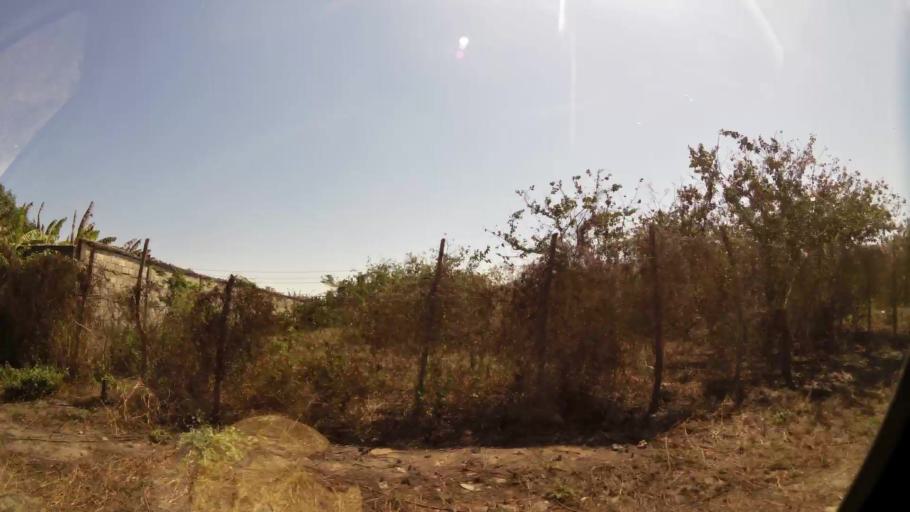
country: CO
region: Atlantico
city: Barranquilla
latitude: 10.9845
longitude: -74.7680
